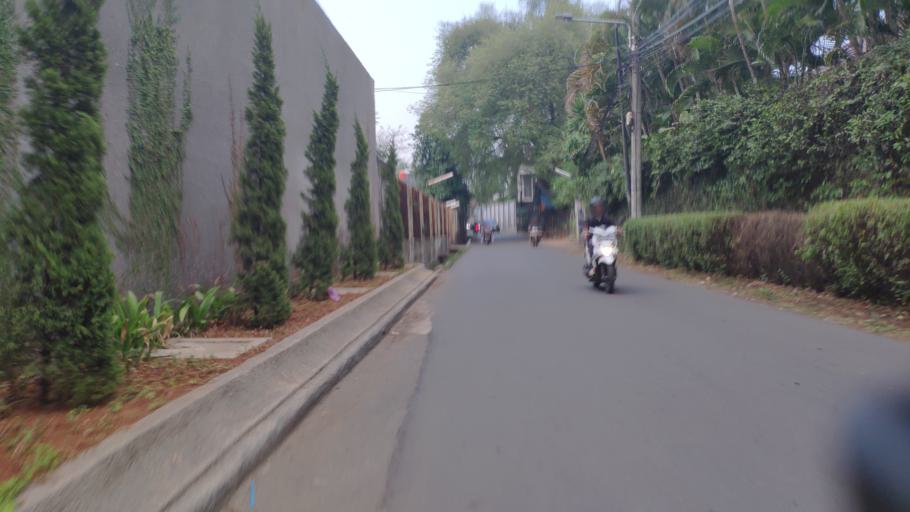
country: ID
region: West Java
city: Pamulang
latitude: -6.2975
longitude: 106.8005
